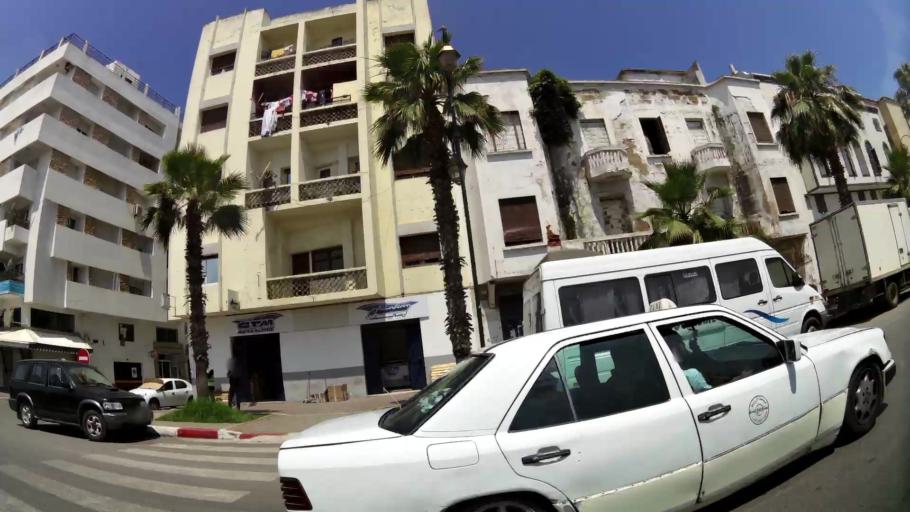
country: MA
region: Rabat-Sale-Zemmour-Zaer
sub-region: Rabat
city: Rabat
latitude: 34.0246
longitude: -6.8444
